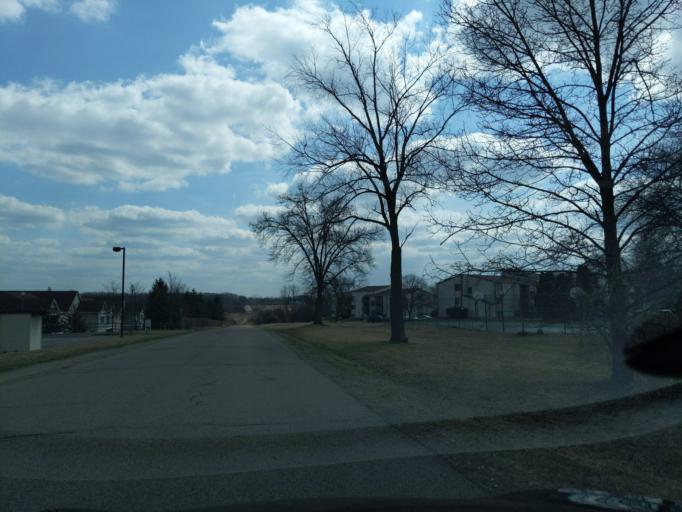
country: US
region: Michigan
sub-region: Jackson County
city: Jackson
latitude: 42.2749
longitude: -84.4429
